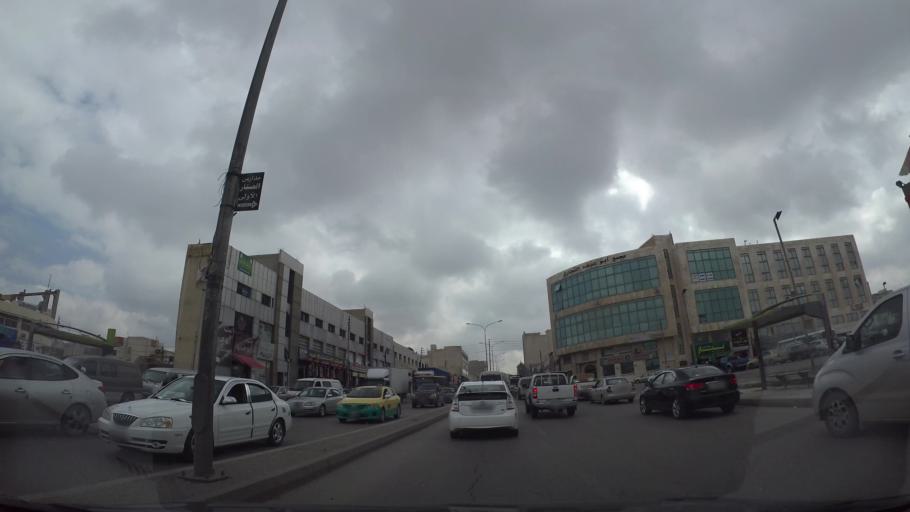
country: JO
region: Amman
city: Al Quwaysimah
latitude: 31.9123
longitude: 35.9388
